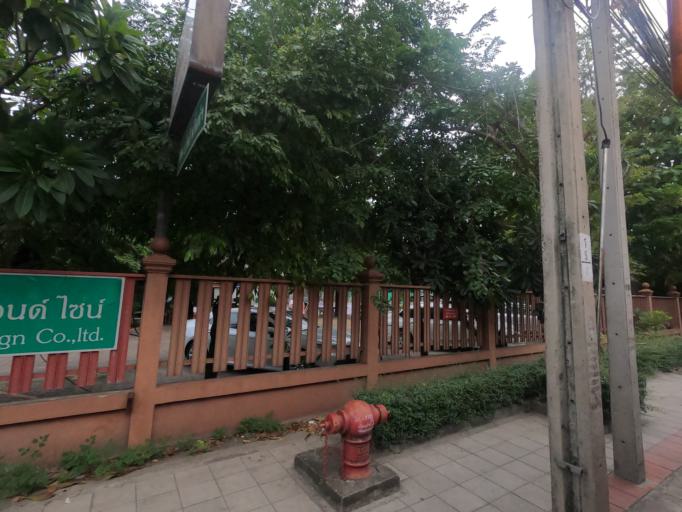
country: TH
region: Bangkok
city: Lat Phrao
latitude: 13.7965
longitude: 100.6070
